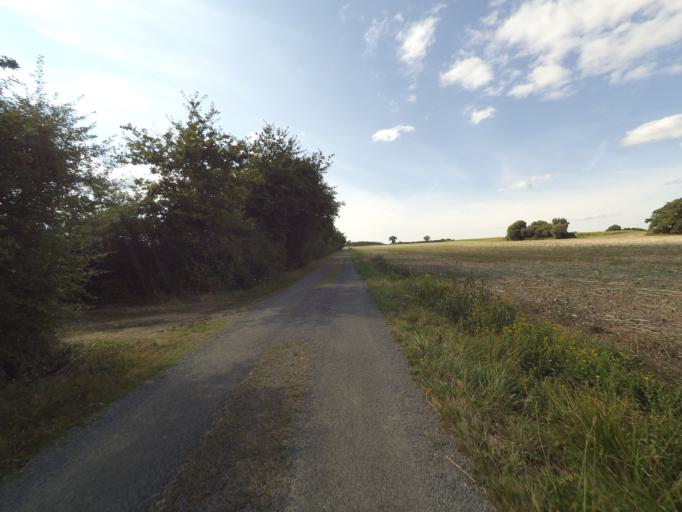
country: FR
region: Pays de la Loire
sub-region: Departement de la Loire-Atlantique
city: Vieillevigne
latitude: 46.9558
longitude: -1.4417
